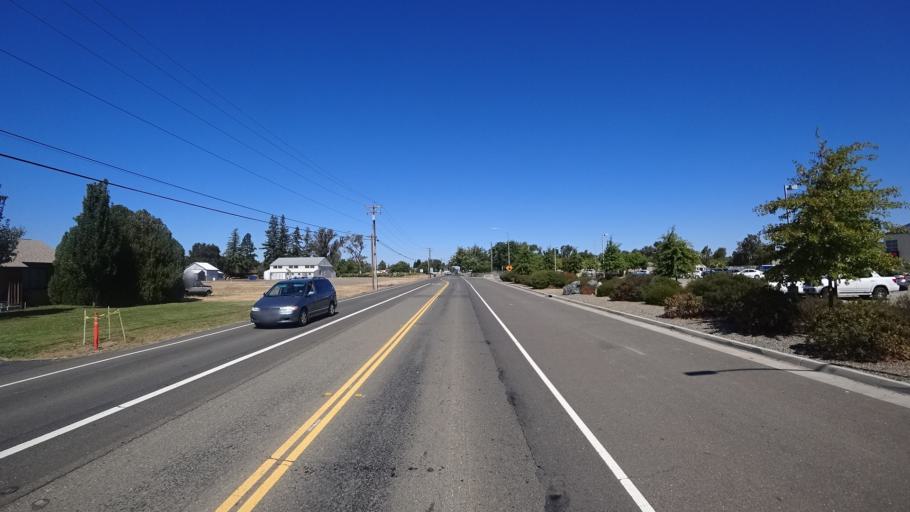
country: US
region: California
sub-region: Sacramento County
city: Elk Grove
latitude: 38.4070
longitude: -121.3346
